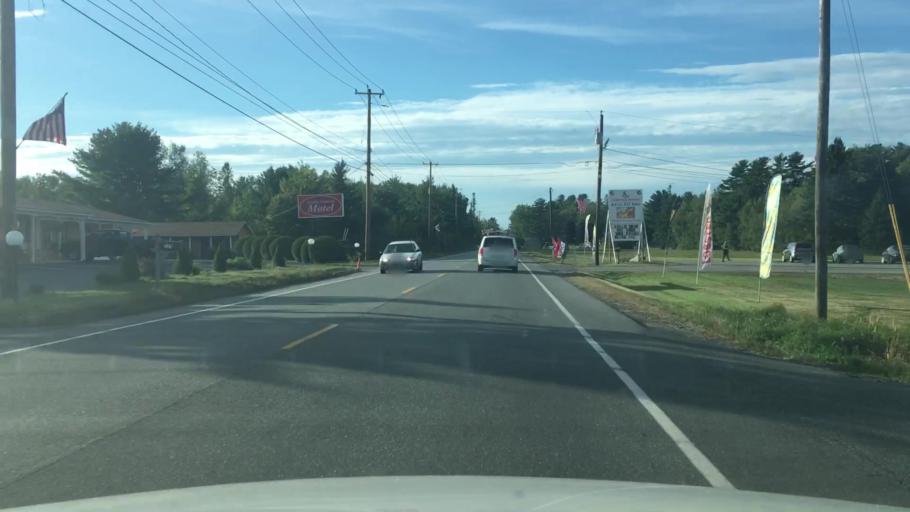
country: US
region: Maine
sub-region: Hancock County
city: Trenton
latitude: 44.4910
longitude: -68.3734
